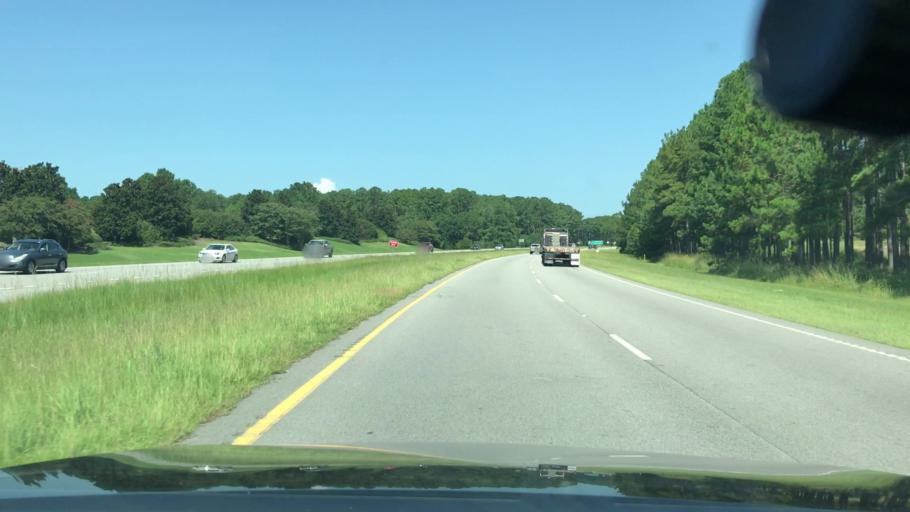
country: US
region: South Carolina
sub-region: Jasper County
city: Hardeeville
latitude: 32.3020
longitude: -80.9662
